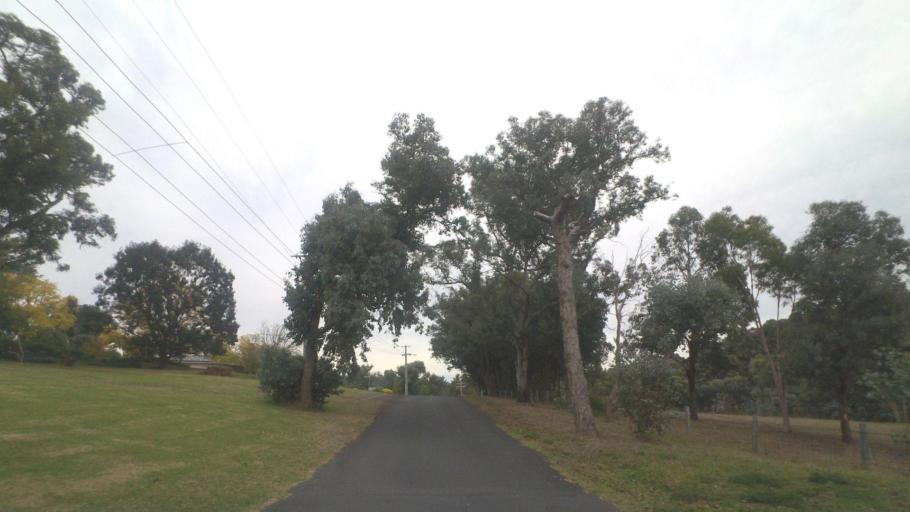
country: AU
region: Victoria
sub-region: Nillumbik
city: North Warrandyte
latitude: -37.7409
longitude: 145.1850
